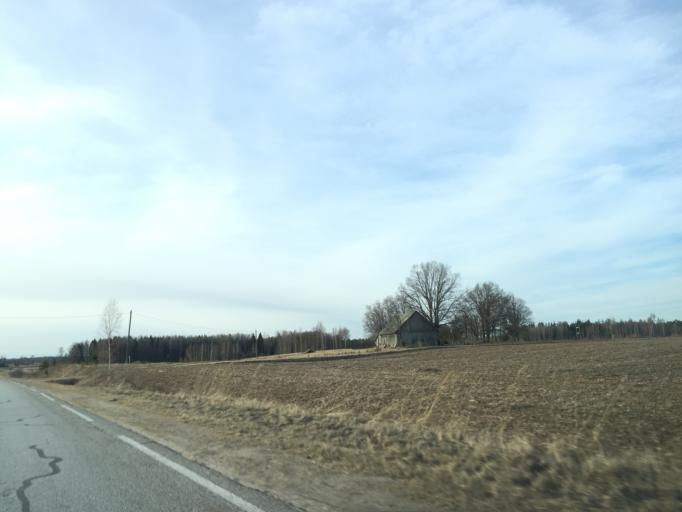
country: LV
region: Krimulda
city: Ragana
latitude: 57.1687
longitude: 24.7392
